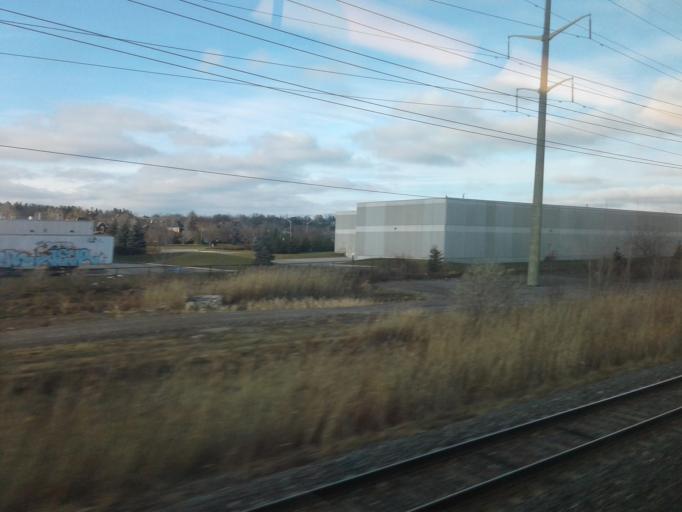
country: CA
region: Ontario
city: Oakville
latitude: 43.4956
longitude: -79.6495
